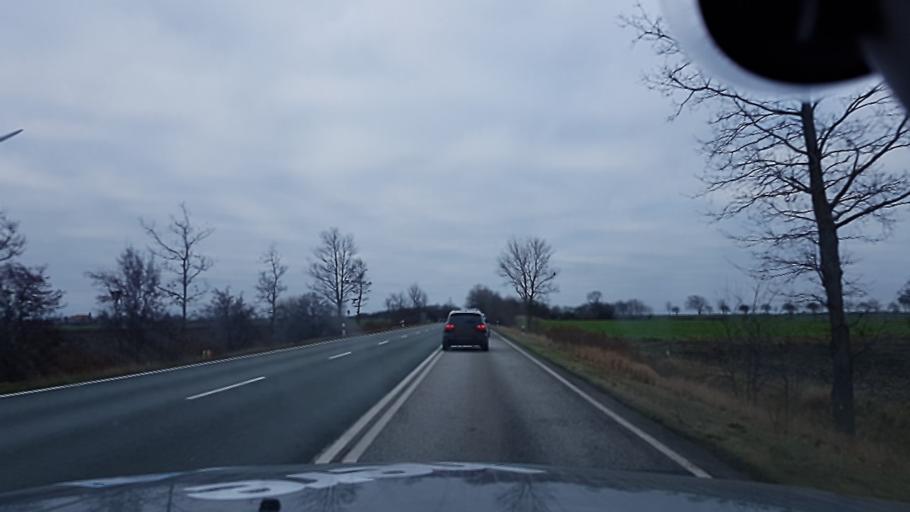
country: DE
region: Schleswig-Holstein
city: Fehmarn
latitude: 54.4843
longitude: 11.2142
